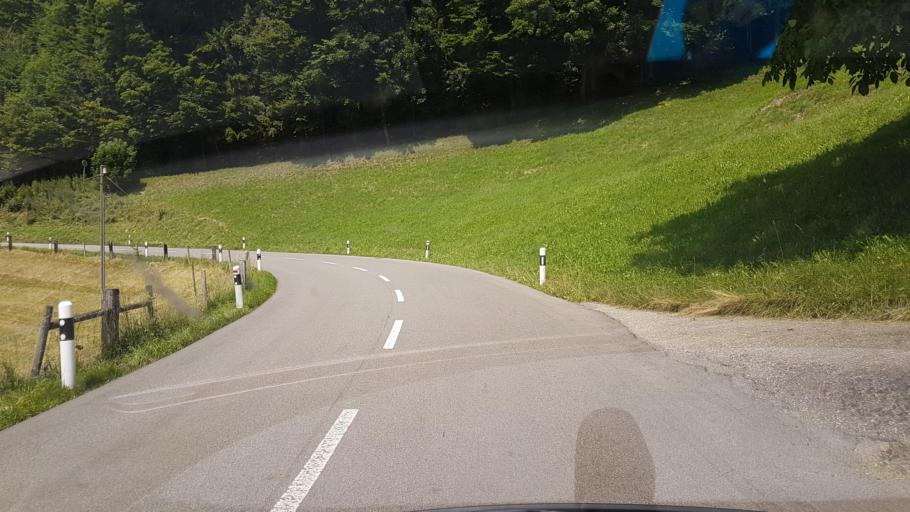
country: CH
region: Saint Gallen
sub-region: Wahlkreis Toggenburg
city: Oberhelfenschwil
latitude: 47.3274
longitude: 9.1207
